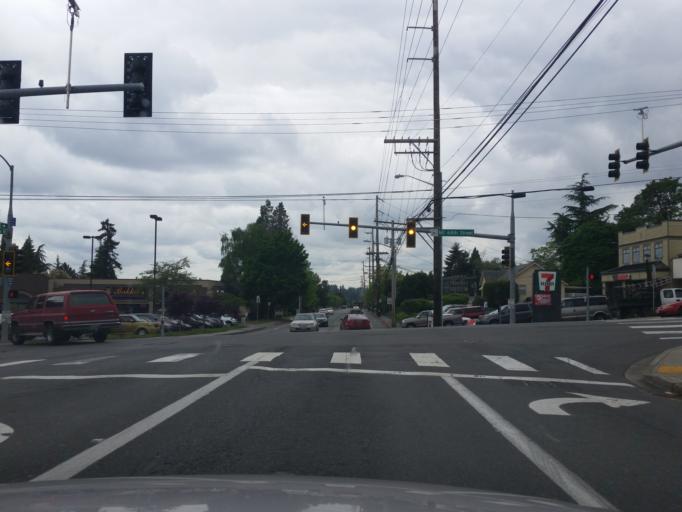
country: US
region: Washington
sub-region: King County
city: Kirkland
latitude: 47.6666
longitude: -122.1962
